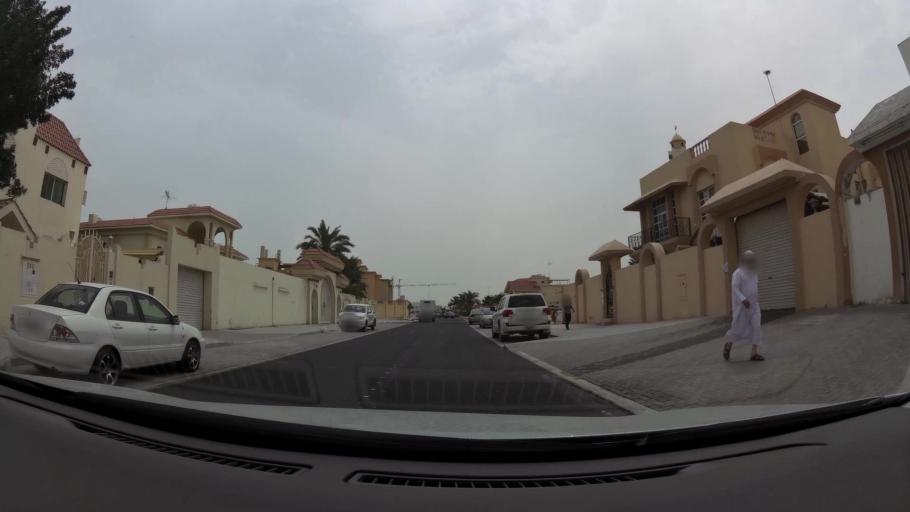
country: QA
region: Baladiyat ad Dawhah
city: Doha
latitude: 25.2441
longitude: 51.5607
